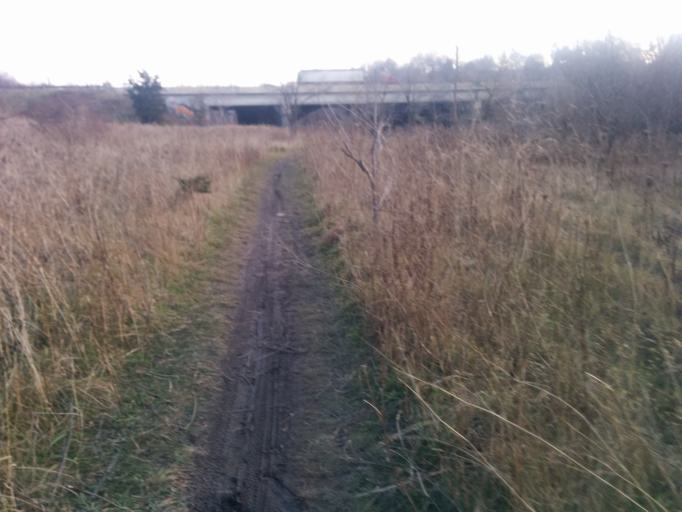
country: CA
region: Ontario
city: Etobicoke
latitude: 43.6058
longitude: -79.5605
